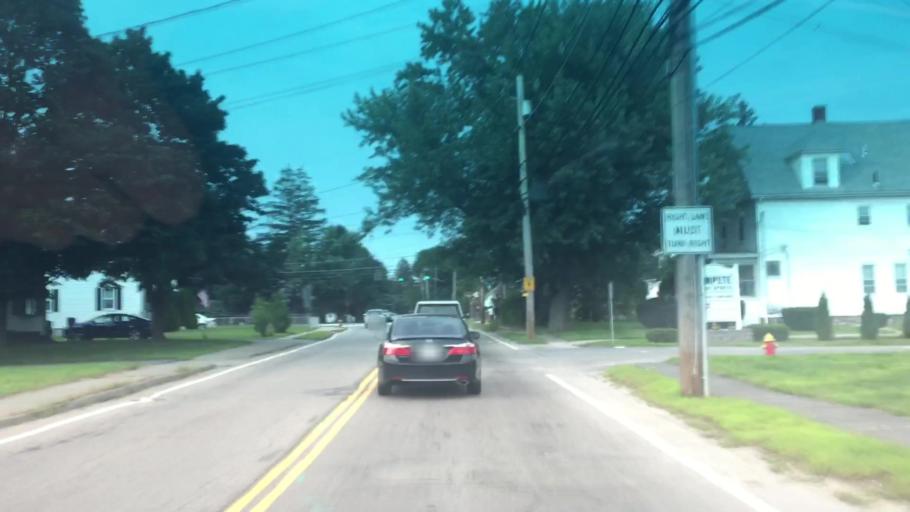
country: US
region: Massachusetts
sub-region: Norfolk County
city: Norwood
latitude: 42.1782
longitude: -71.1992
